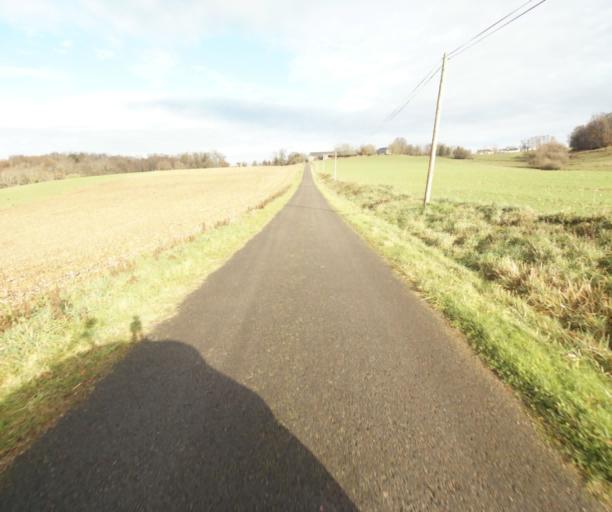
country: FR
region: Limousin
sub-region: Departement de la Correze
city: Sainte-Fereole
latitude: 45.2763
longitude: 1.5974
